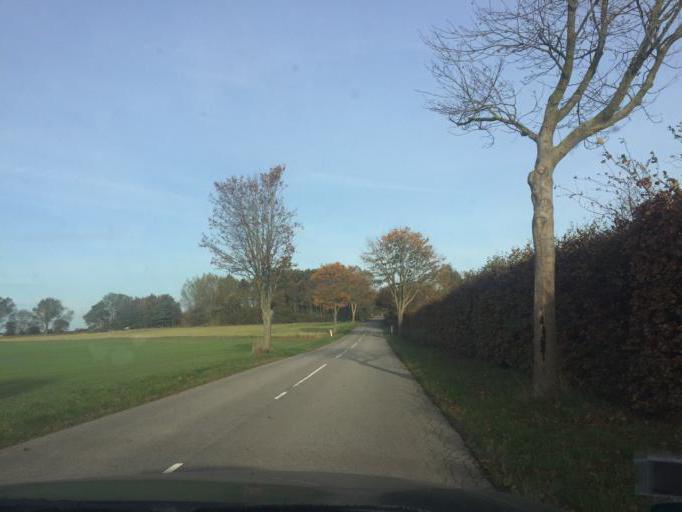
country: DK
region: Zealand
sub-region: Stevns Kommune
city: Store Heddinge
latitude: 55.2753
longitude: 12.4233
